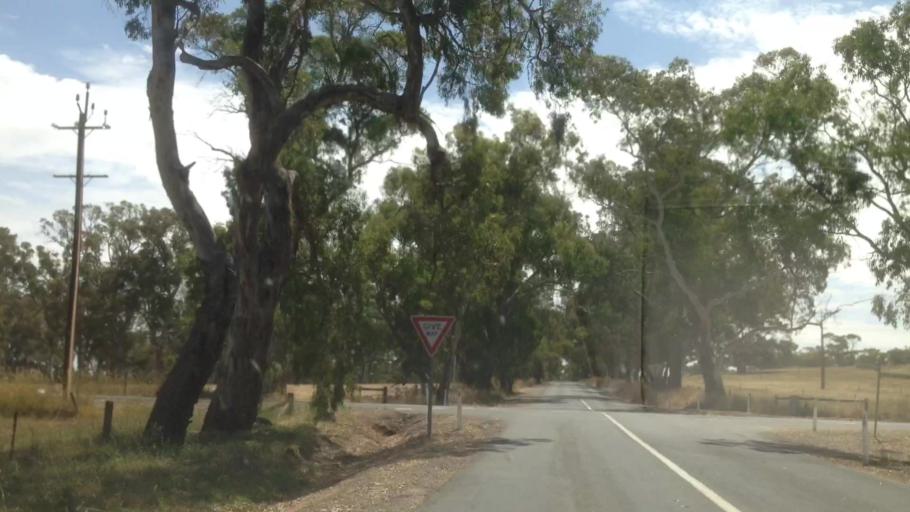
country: AU
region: South Australia
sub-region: Adelaide Hills
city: Birdwood
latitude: -34.7907
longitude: 138.9551
